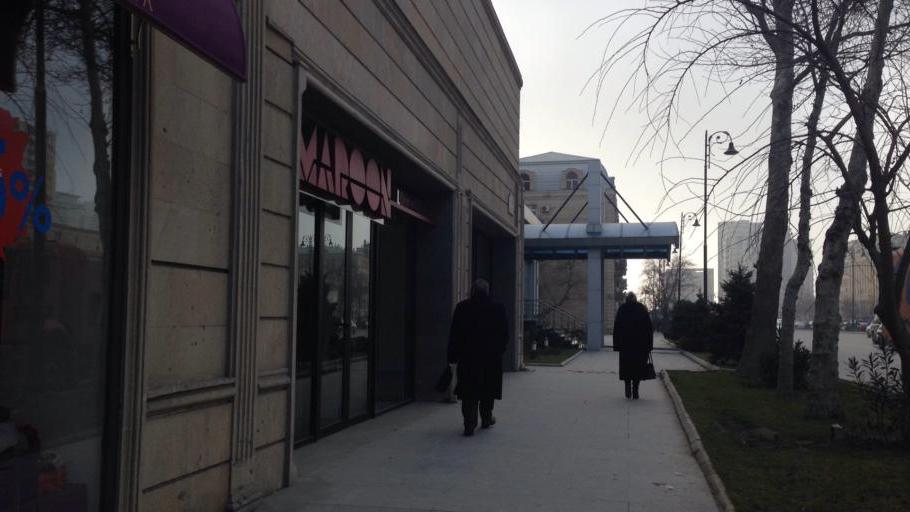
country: AZ
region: Baki
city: Baku
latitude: 40.3837
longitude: 49.8640
